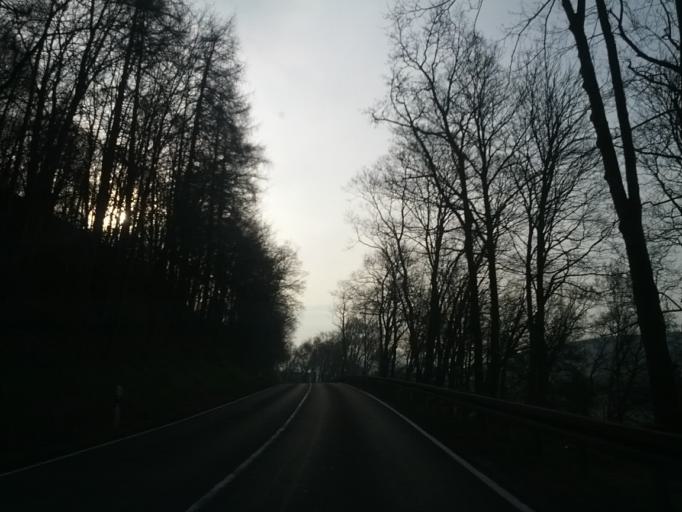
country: DE
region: Thuringia
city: Schwallungen
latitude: 50.6764
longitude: 10.3526
